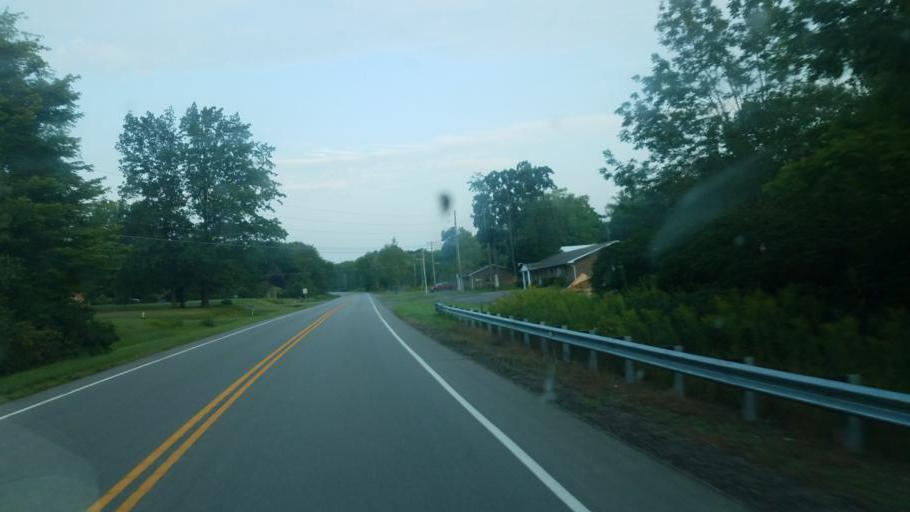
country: US
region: Pennsylvania
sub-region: Crawford County
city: Conneaut Lakeshore
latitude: 41.6039
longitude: -80.3319
